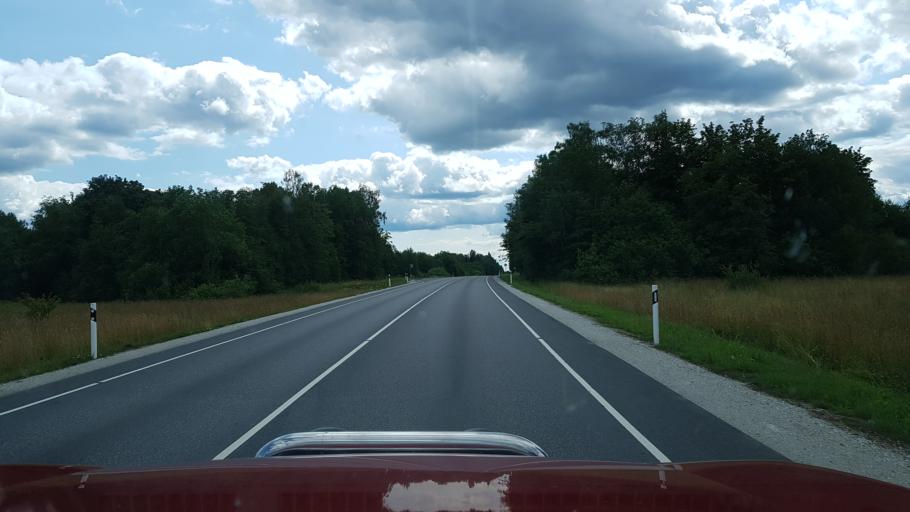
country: EE
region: Ida-Virumaa
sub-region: Johvi vald
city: Johvi
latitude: 59.2857
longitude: 27.3976
